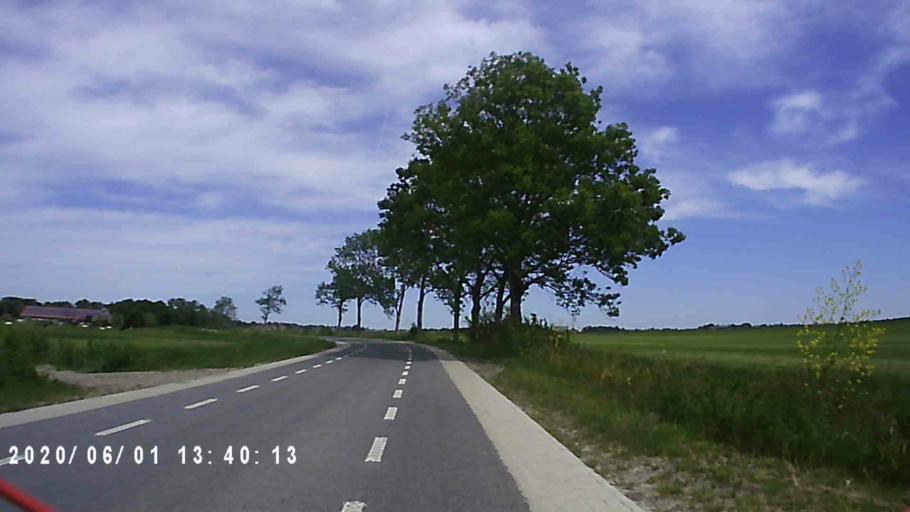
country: NL
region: Friesland
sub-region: Gemeente Littenseradiel
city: Wommels
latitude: 53.0886
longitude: 5.6023
